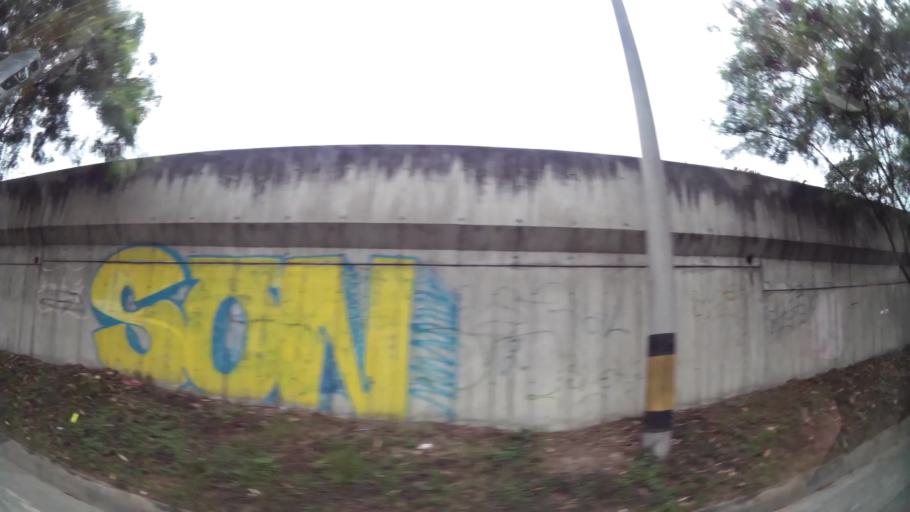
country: CO
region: Antioquia
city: Bello
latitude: 6.3072
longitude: -75.5583
